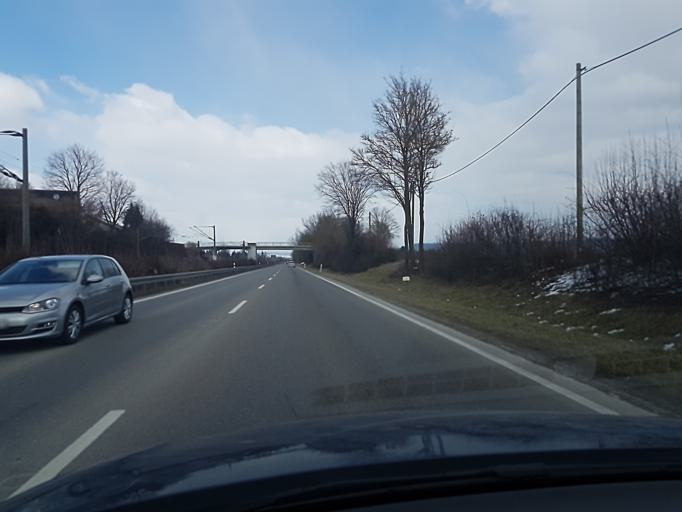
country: DE
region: Baden-Wuerttemberg
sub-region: Regierungsbezirk Stuttgart
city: Herrenberg
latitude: 48.5638
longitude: 8.8536
